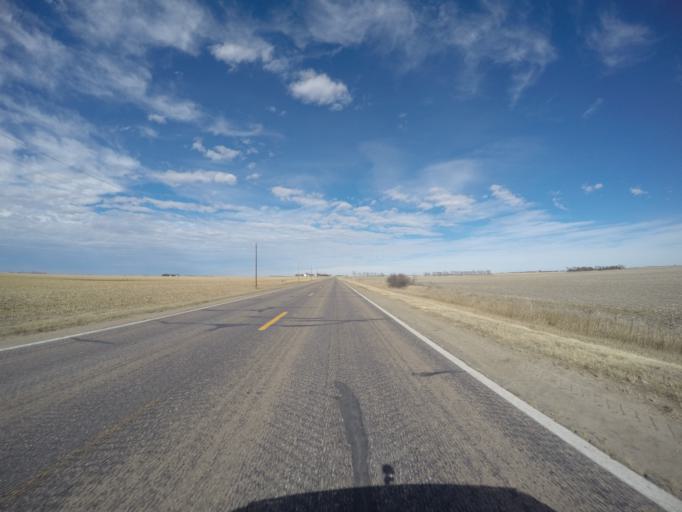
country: US
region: Nebraska
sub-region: Franklin County
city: Franklin
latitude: 40.2654
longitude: -98.9523
